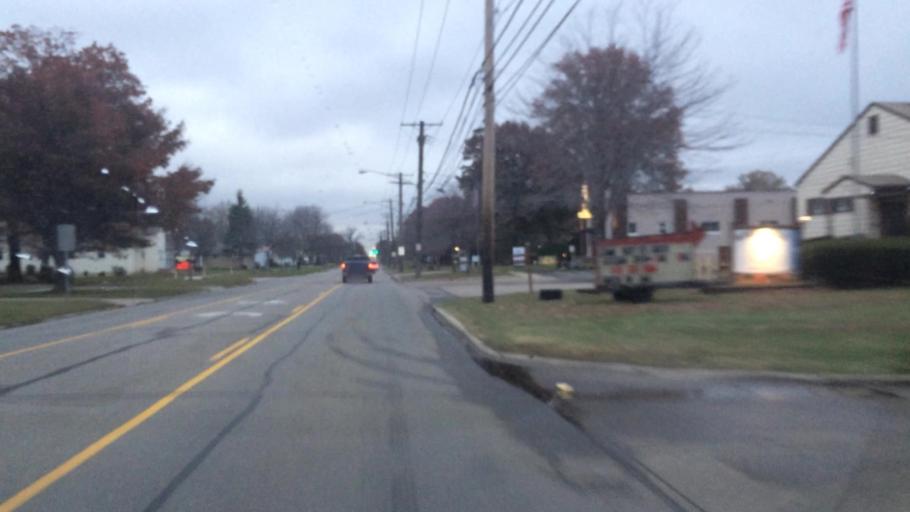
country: US
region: Ohio
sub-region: Cuyahoga County
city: Berea
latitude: 41.3816
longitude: -81.8579
